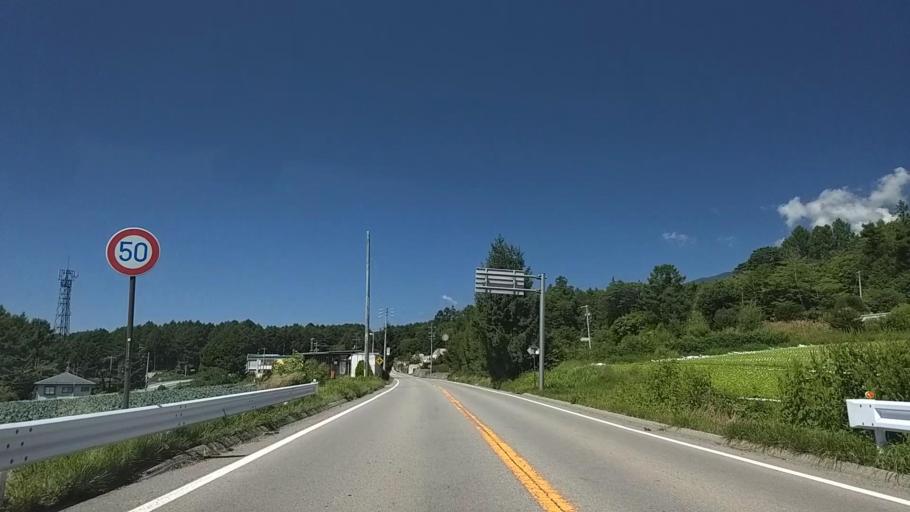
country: JP
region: Nagano
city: Komoro
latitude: 36.3380
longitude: 138.5042
